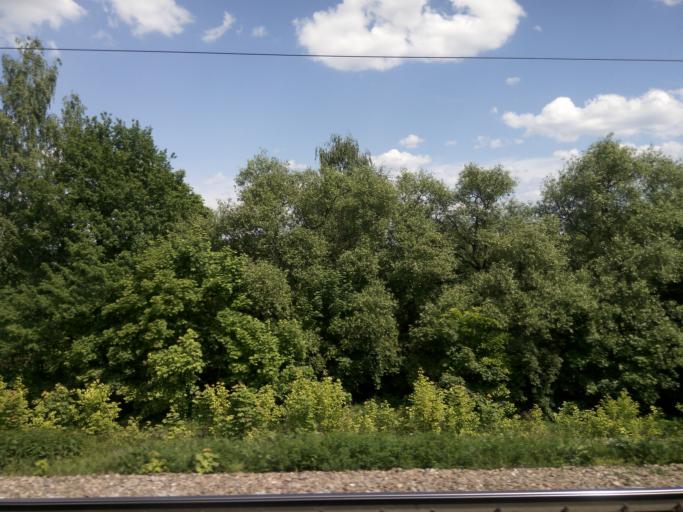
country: RU
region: Moscow
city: Zagor'ye
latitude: 55.5624
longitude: 37.6714
